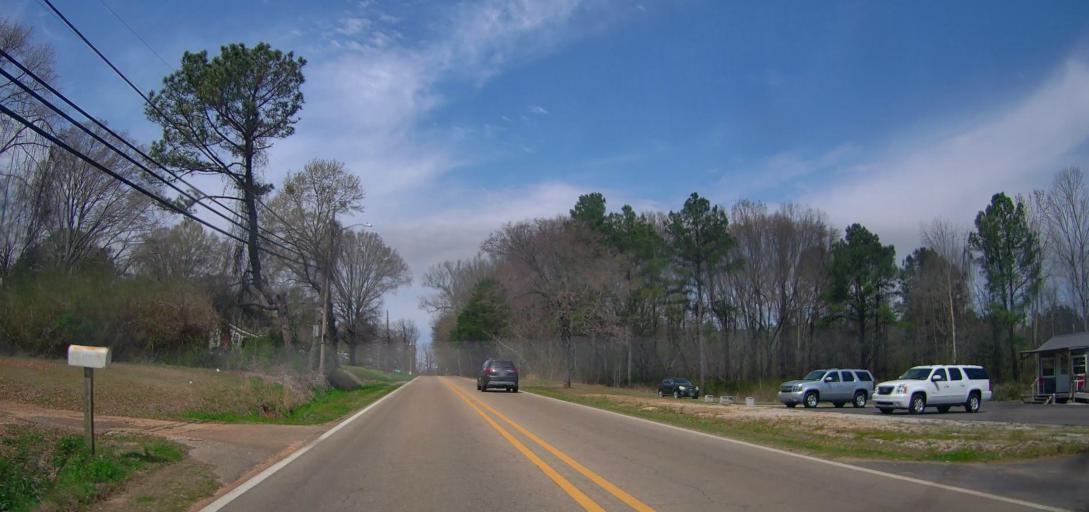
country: US
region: Mississippi
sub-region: Union County
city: New Albany
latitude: 34.4756
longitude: -88.9957
